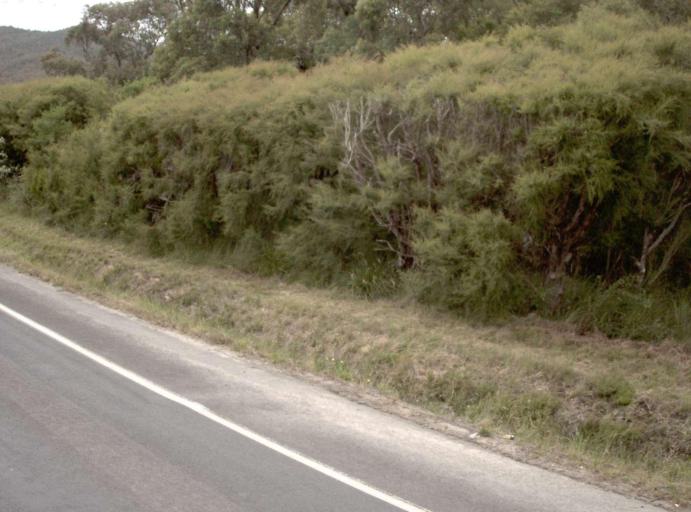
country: AU
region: Victoria
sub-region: Yarra Ranges
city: Millgrove
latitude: -37.7736
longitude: 145.6454
